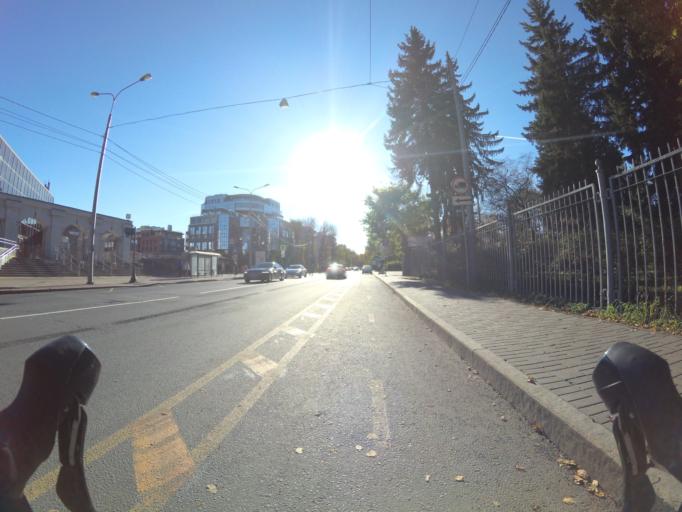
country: RU
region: Leningrad
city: Krestovskiy ostrov
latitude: 59.9719
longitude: 30.2587
